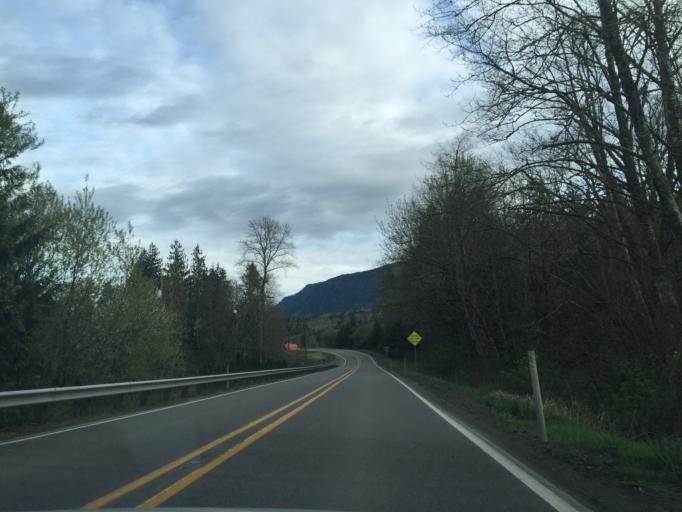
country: US
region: Washington
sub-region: Snohomish County
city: Arlington Heights
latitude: 48.2742
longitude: -121.9039
